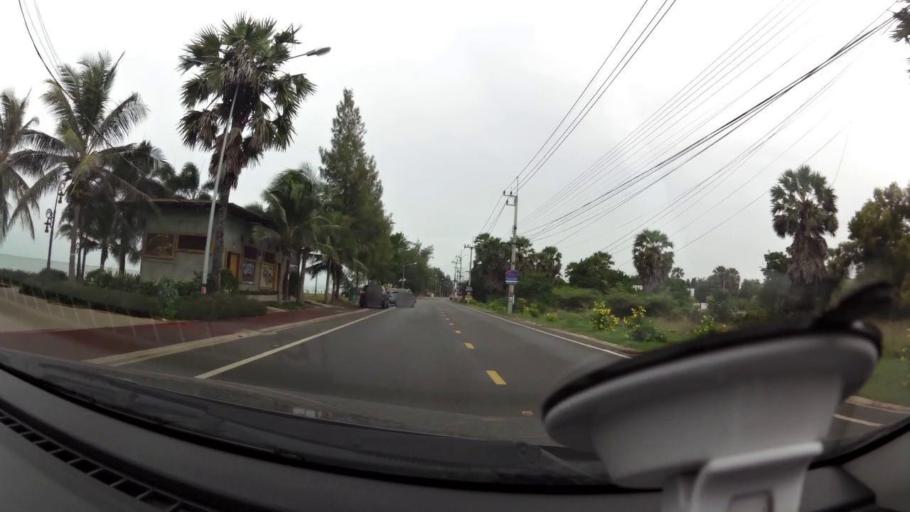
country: TH
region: Prachuap Khiri Khan
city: Pran Buri
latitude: 12.3705
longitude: 100.0000
